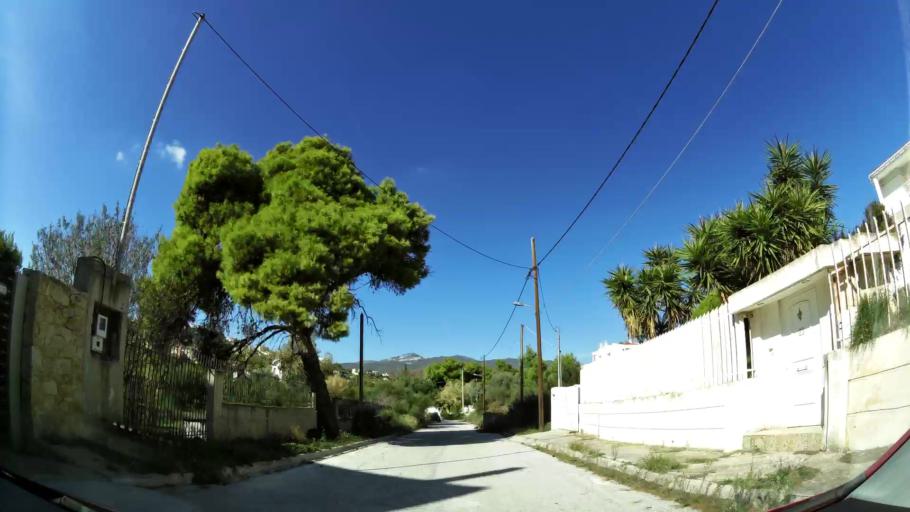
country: GR
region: Attica
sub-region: Nomarchia Anatolikis Attikis
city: Dhrafi
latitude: 38.0168
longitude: 23.9116
